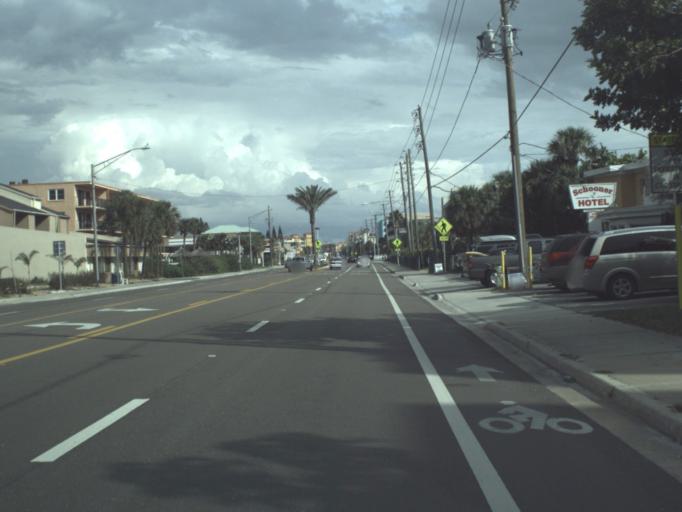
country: US
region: Florida
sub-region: Pinellas County
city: Madeira Beach
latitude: 27.7984
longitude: -82.7981
